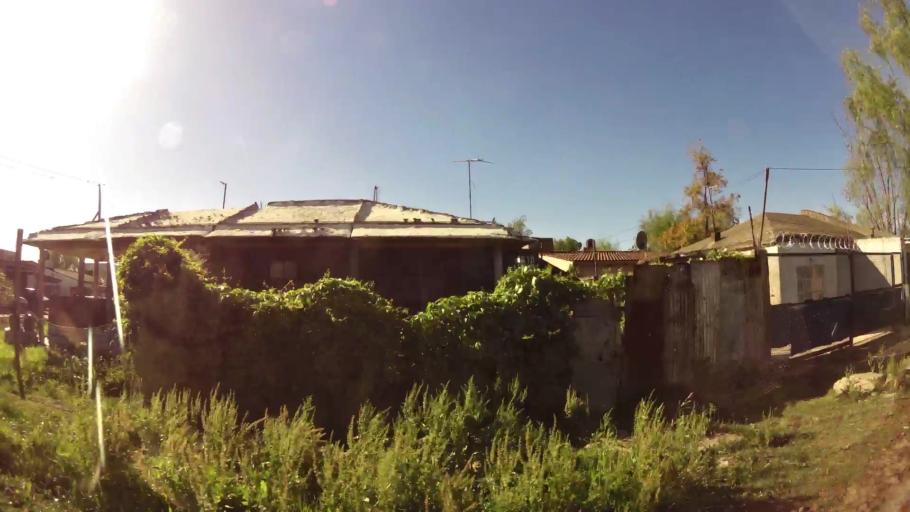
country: AR
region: Buenos Aires
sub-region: Partido de Quilmes
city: Quilmes
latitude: -34.7575
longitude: -58.3147
